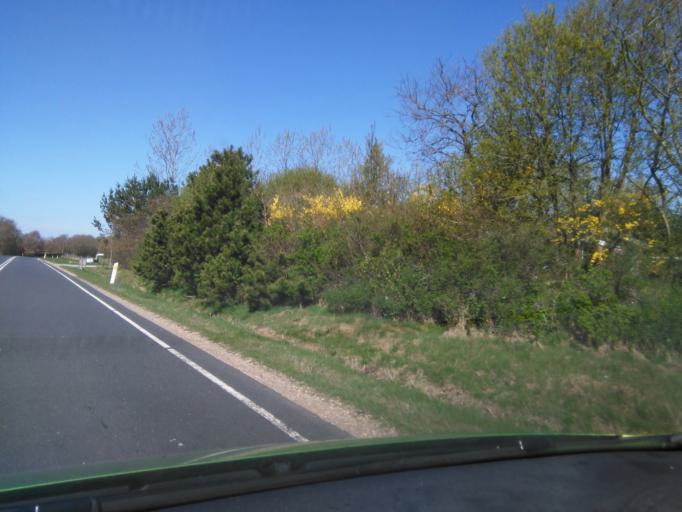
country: DK
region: South Denmark
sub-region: Billund Kommune
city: Grindsted
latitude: 55.7025
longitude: 8.7656
